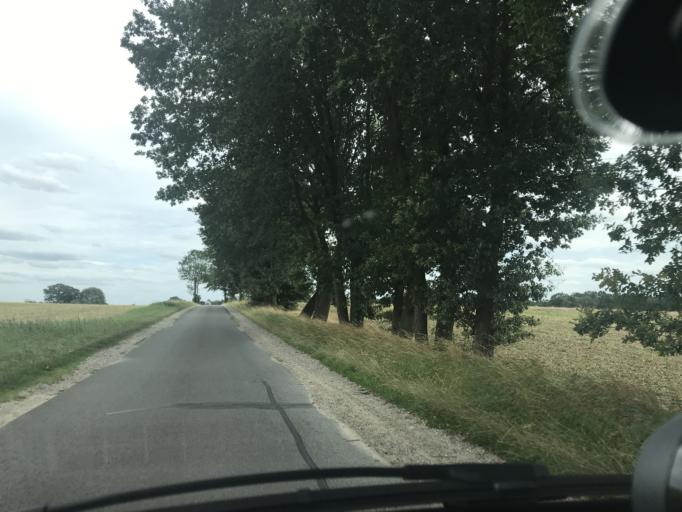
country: DE
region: Lower Saxony
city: Moisburg
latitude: 53.4009
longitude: 9.7154
